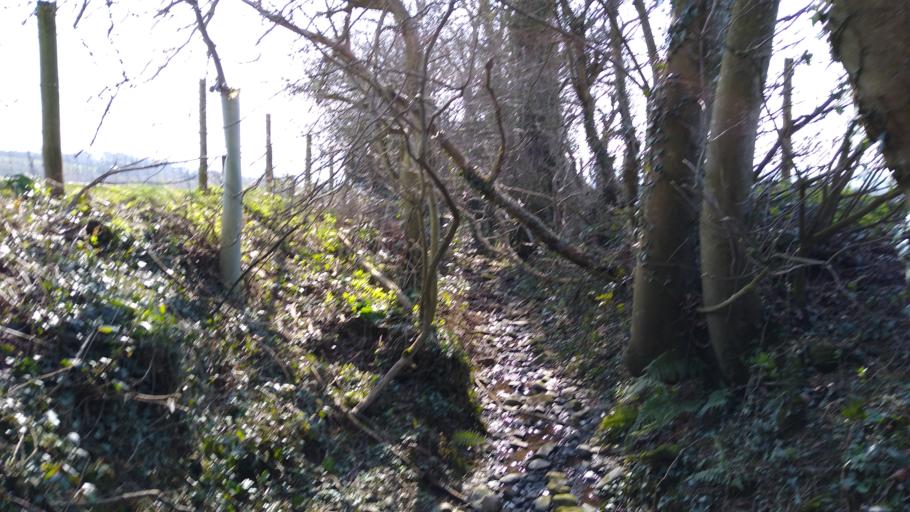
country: GB
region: England
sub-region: Cumbria
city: Cockermouth
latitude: 54.6731
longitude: -3.3915
